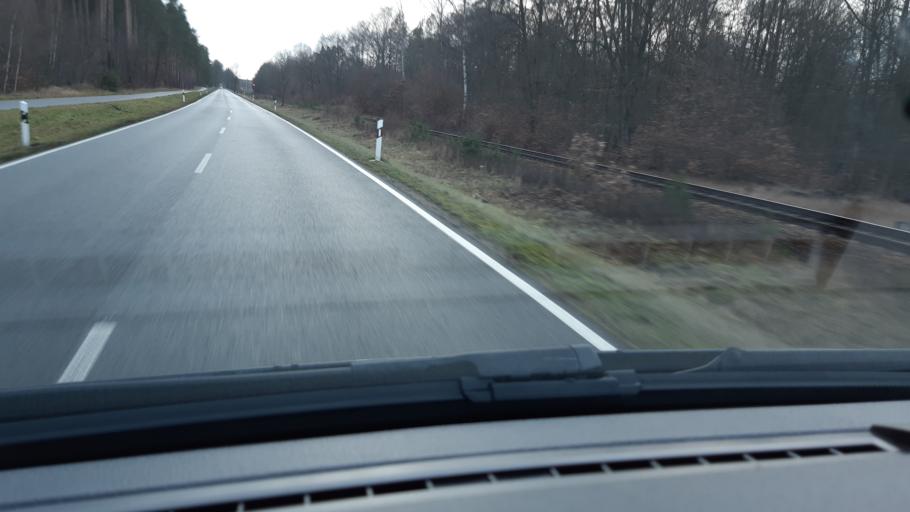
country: DE
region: Brandenburg
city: Zehdenick
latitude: 53.0462
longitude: 13.3921
